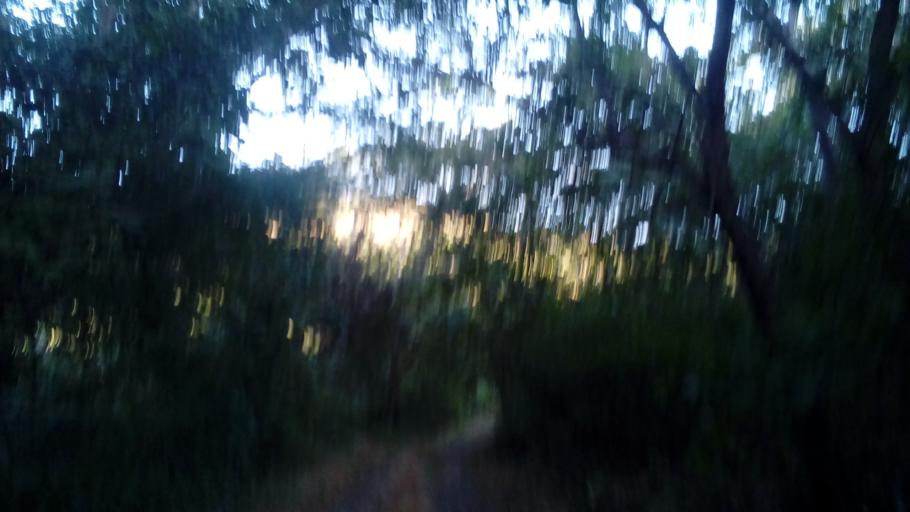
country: CR
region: Guanacaste
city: Sardinal
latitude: 10.3930
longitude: -85.8309
